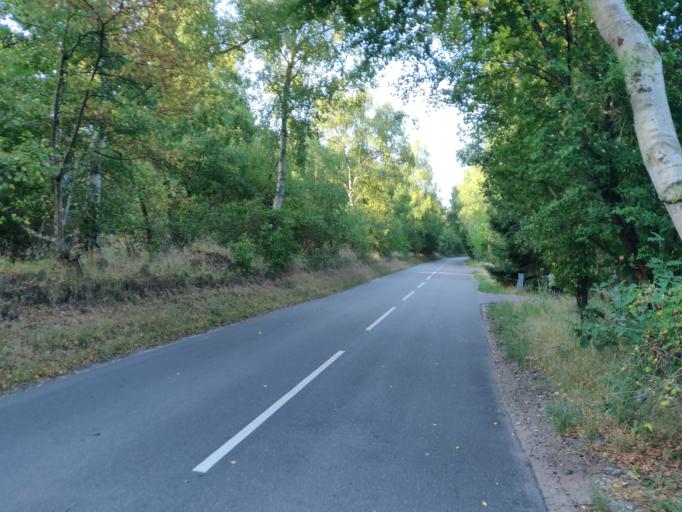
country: DK
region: Zealand
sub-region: Odsherred Kommune
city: Hojby
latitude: 55.8888
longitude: 11.5434
